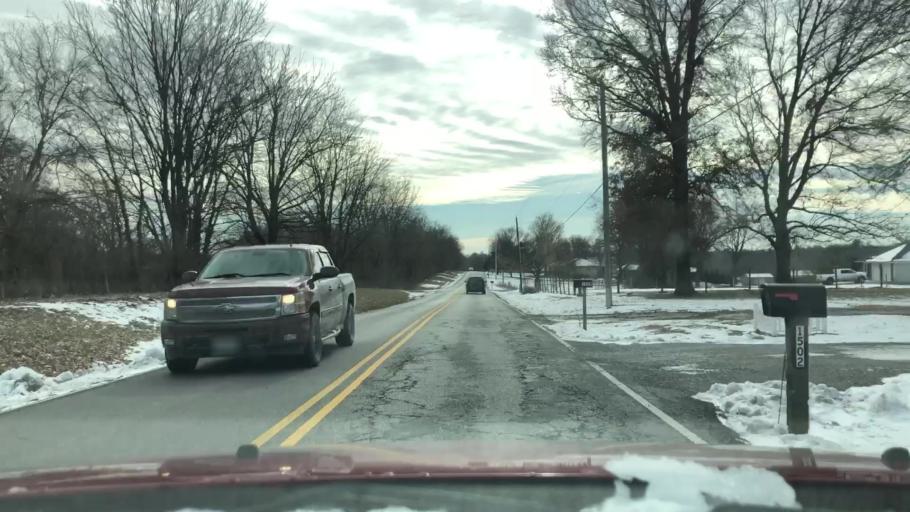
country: US
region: Missouri
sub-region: Jackson County
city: Greenwood
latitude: 38.8641
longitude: -94.3420
